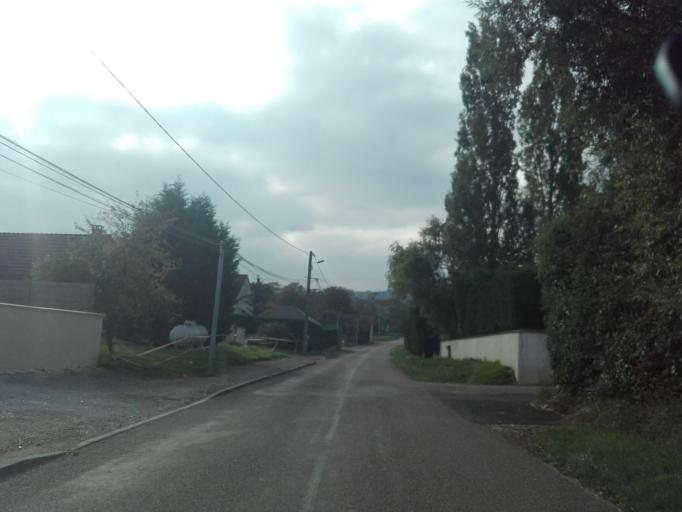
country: FR
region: Bourgogne
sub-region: Departement de Saone-et-Loire
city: Rully
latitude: 46.8815
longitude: 4.7707
